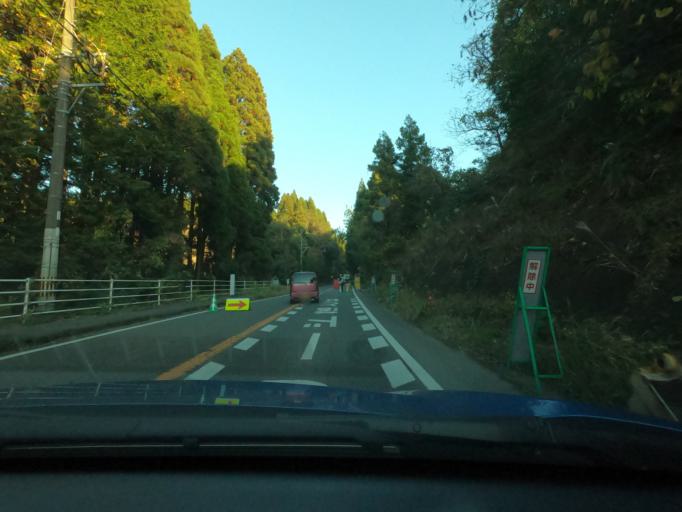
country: JP
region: Kagoshima
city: Satsumasendai
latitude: 31.8137
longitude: 130.3752
